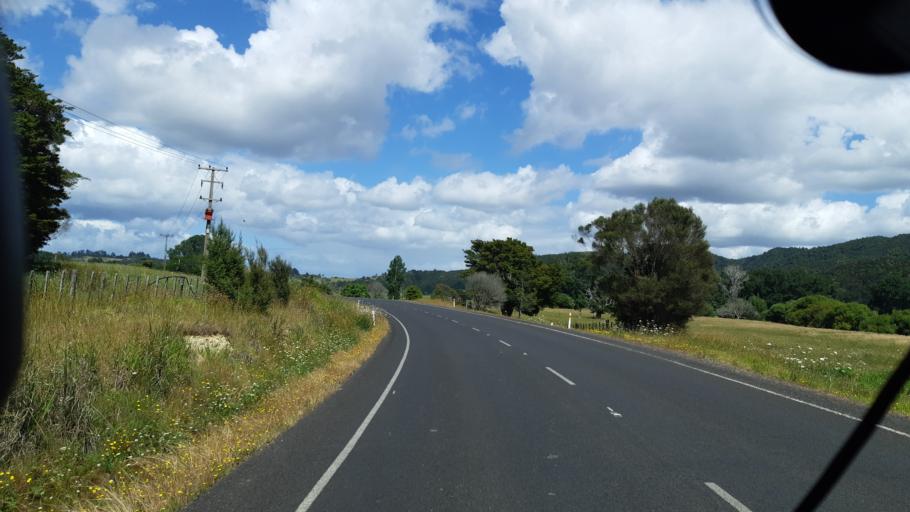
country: NZ
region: Northland
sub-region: Far North District
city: Waimate North
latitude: -35.2926
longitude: 173.6680
